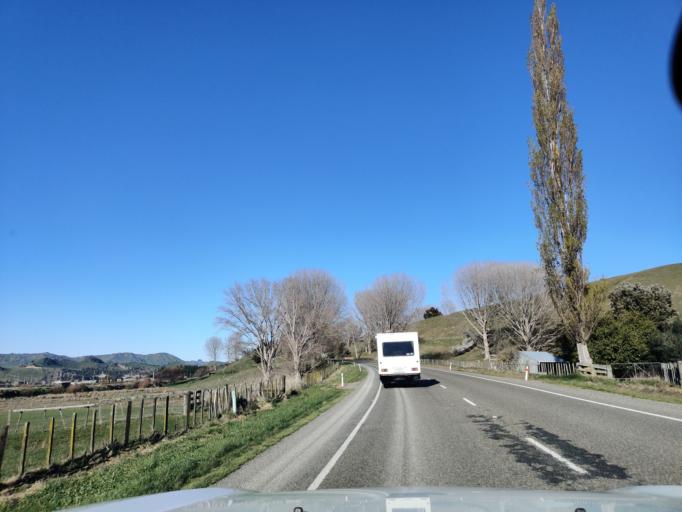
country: NZ
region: Manawatu-Wanganui
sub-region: Ruapehu District
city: Waiouru
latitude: -39.7366
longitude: 175.8413
